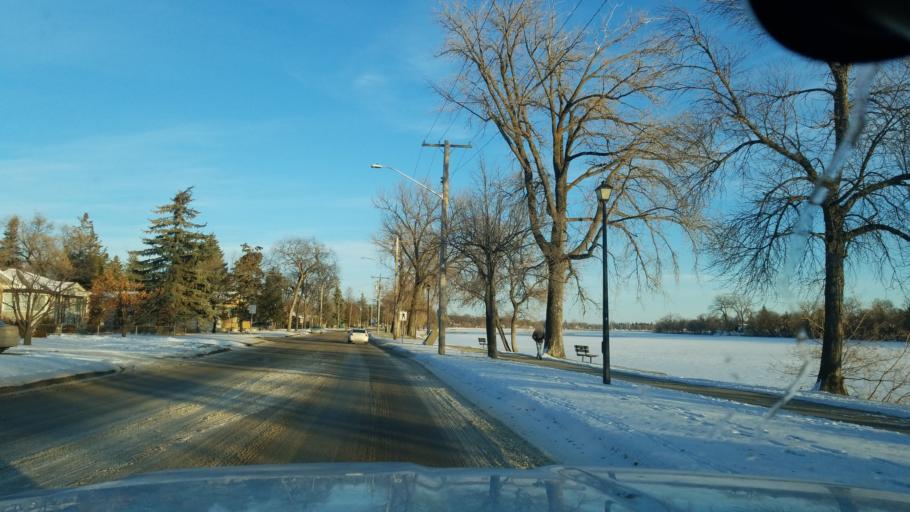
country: CA
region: Manitoba
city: Portage la Prairie
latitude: 49.9703
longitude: -98.3076
